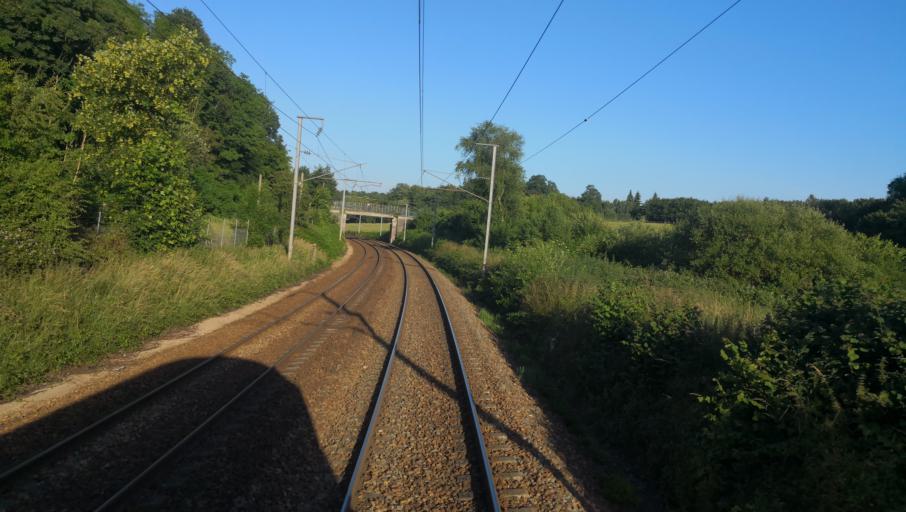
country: FR
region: Haute-Normandie
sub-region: Departement de l'Eure
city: Bernay
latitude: 49.0859
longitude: 0.5682
